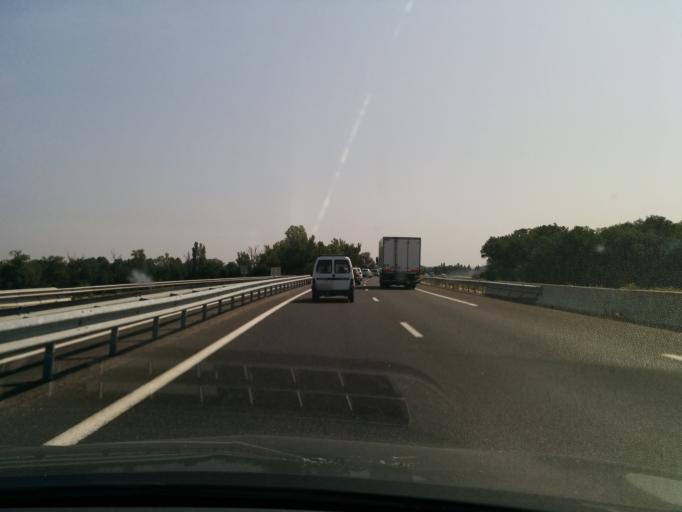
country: FR
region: Midi-Pyrenees
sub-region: Departement du Tarn
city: Marssac-sur-Tarn
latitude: 43.9140
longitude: 2.0546
